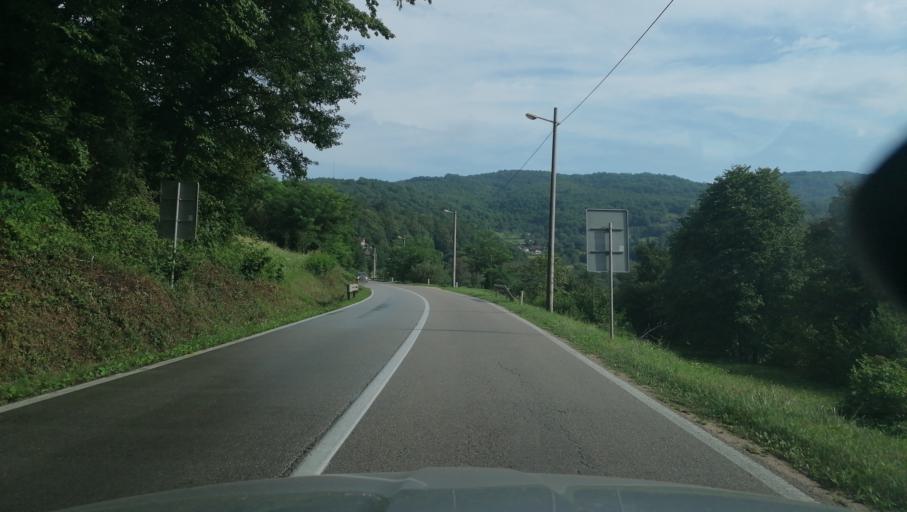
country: BA
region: Republika Srpska
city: Hiseti
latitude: 44.6695
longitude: 17.1455
